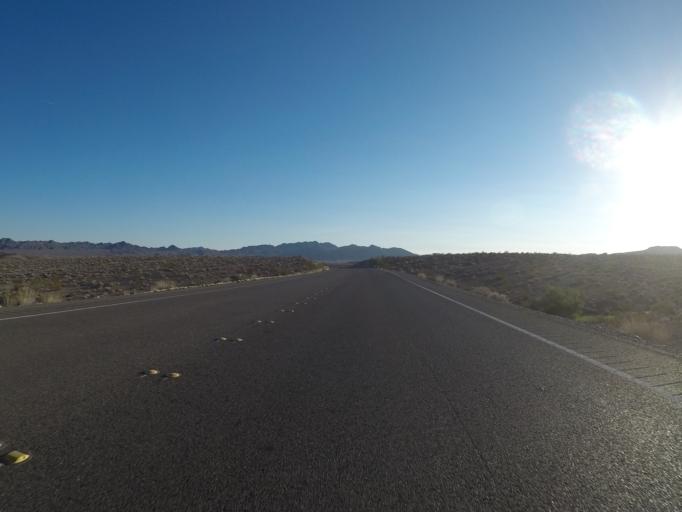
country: US
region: Nevada
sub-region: Clark County
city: Moapa Valley
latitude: 36.3236
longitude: -114.4927
